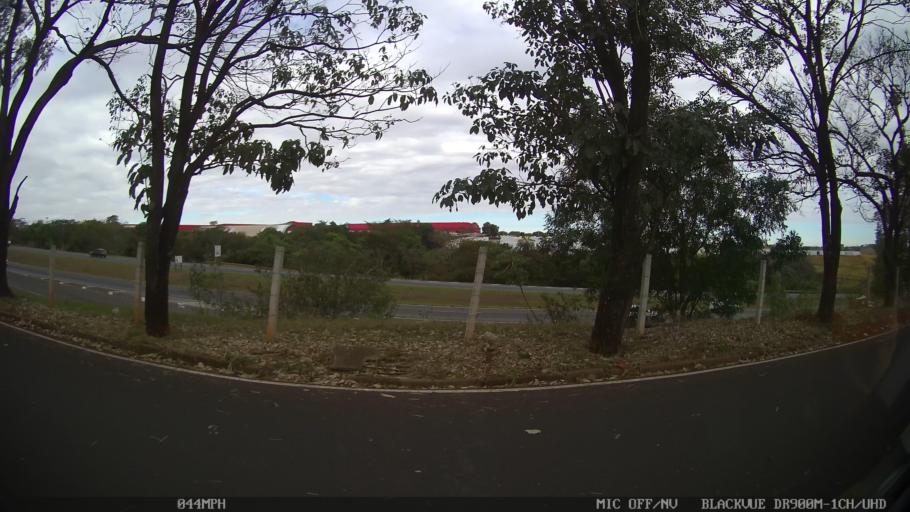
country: BR
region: Sao Paulo
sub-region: Sao Jose Do Rio Preto
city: Sao Jose do Rio Preto
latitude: -20.8213
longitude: -49.4262
